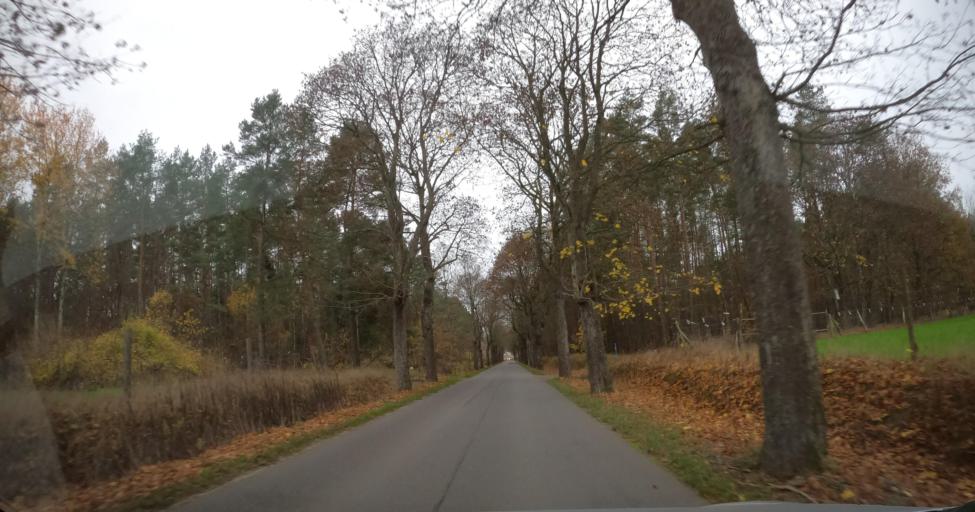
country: PL
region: West Pomeranian Voivodeship
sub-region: Powiat swidwinski
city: Polczyn-Zdroj
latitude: 53.7738
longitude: 16.1579
